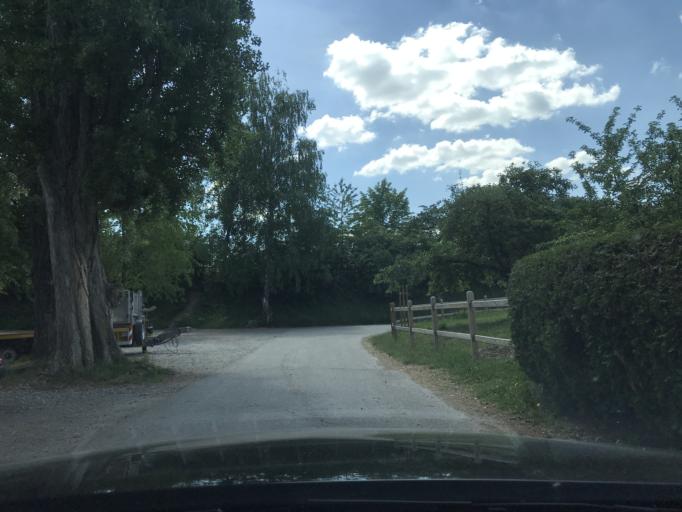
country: DE
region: Baden-Wuerttemberg
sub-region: Regierungsbezirk Stuttgart
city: Weinstadt-Endersbach
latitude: 48.7927
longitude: 9.3773
